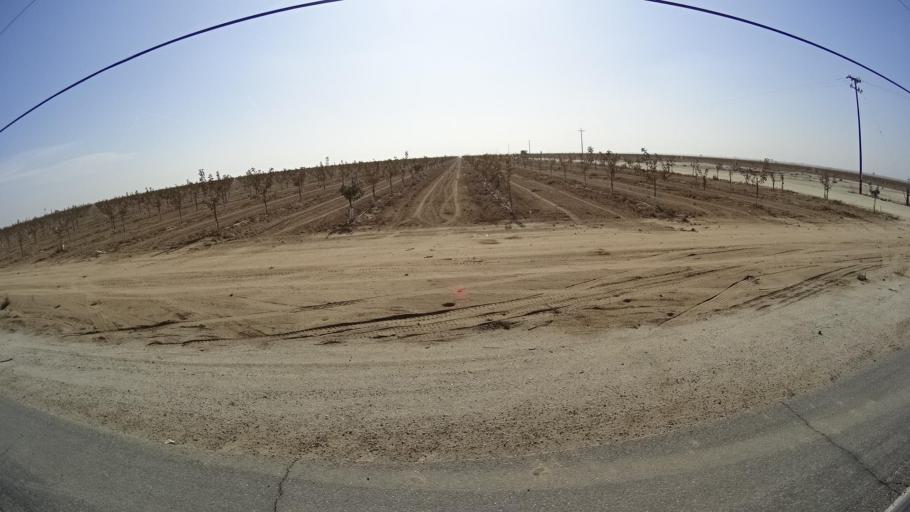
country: US
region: California
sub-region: Kern County
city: Greenacres
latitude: 35.4996
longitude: -119.1255
